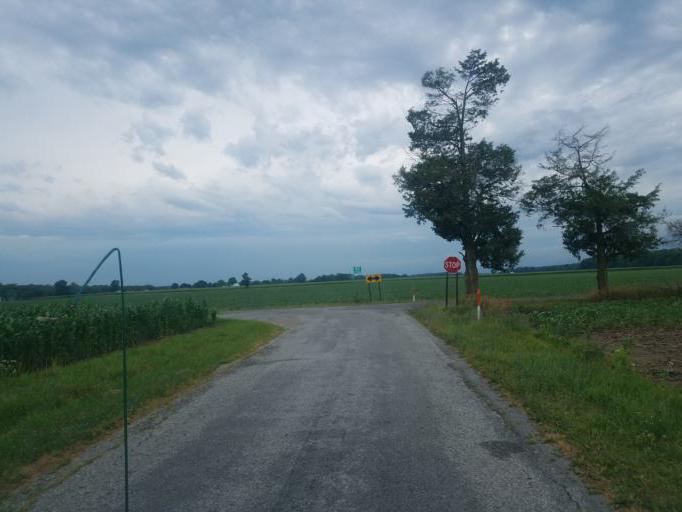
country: US
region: Ohio
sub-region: Paulding County
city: Antwerp
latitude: 41.2410
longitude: -84.7081
